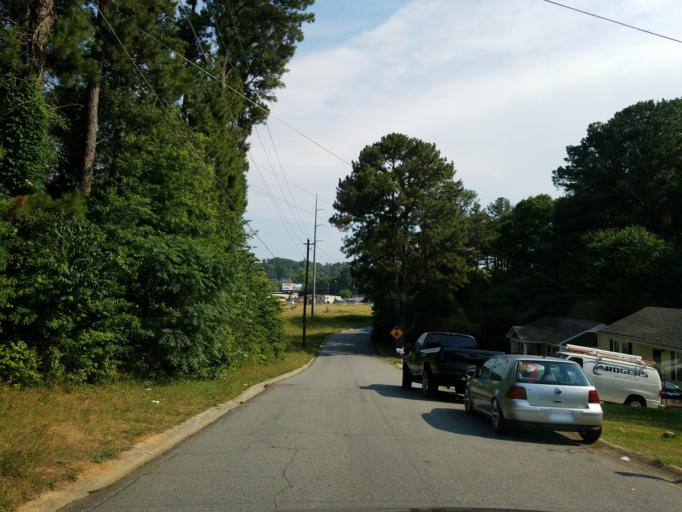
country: US
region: Georgia
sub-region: Cobb County
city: Marietta
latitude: 33.9666
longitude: -84.5324
